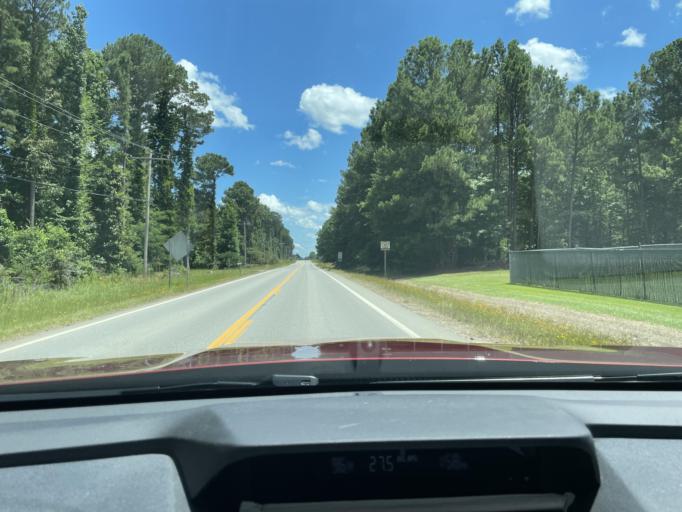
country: US
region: Arkansas
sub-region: Drew County
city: Monticello
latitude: 33.6272
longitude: -91.7552
